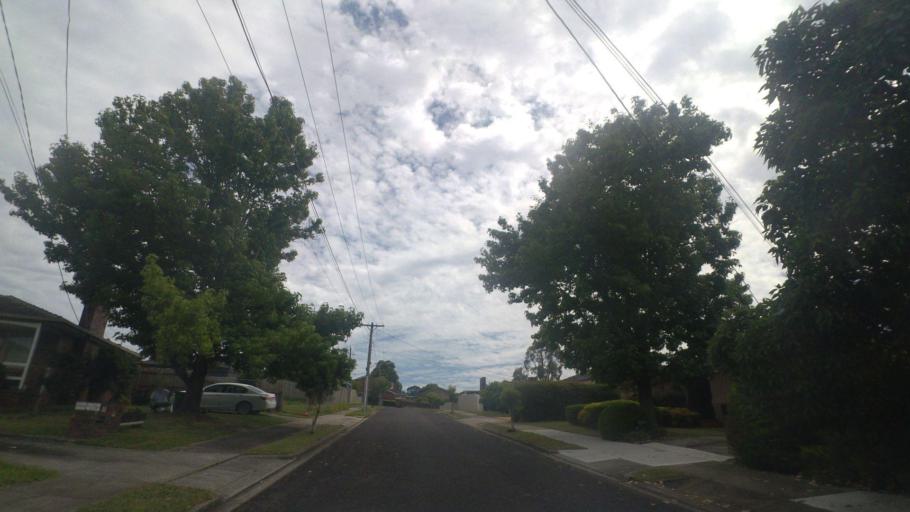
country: AU
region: Victoria
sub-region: Banyule
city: Viewbank
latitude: -37.7406
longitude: 145.0917
